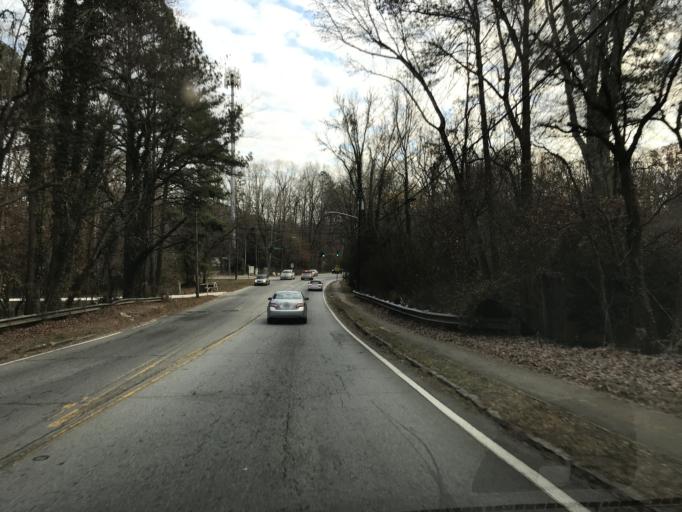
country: US
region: Georgia
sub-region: DeKalb County
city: Tucker
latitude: 33.8728
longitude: -84.2515
